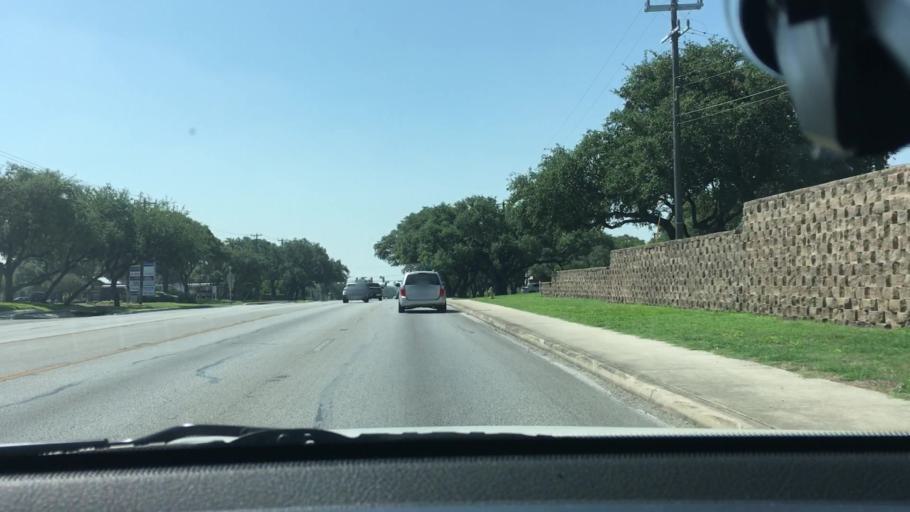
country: US
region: Texas
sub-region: Bexar County
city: Castle Hills
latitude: 29.5351
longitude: -98.5244
